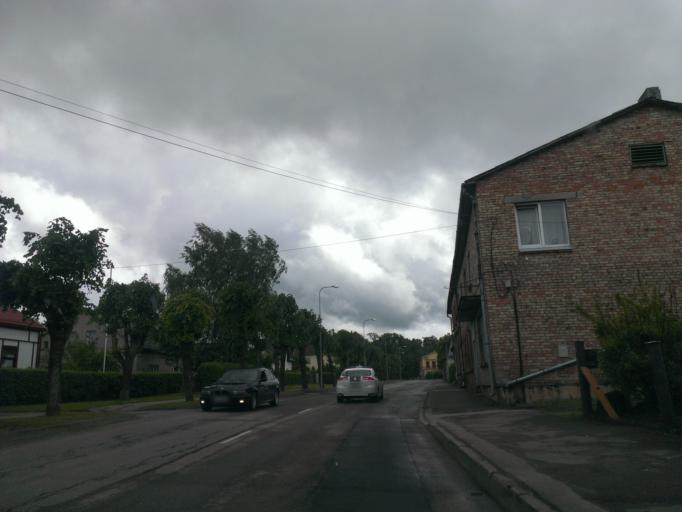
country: LV
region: Grobina
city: Grobina
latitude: 56.5371
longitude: 21.1598
